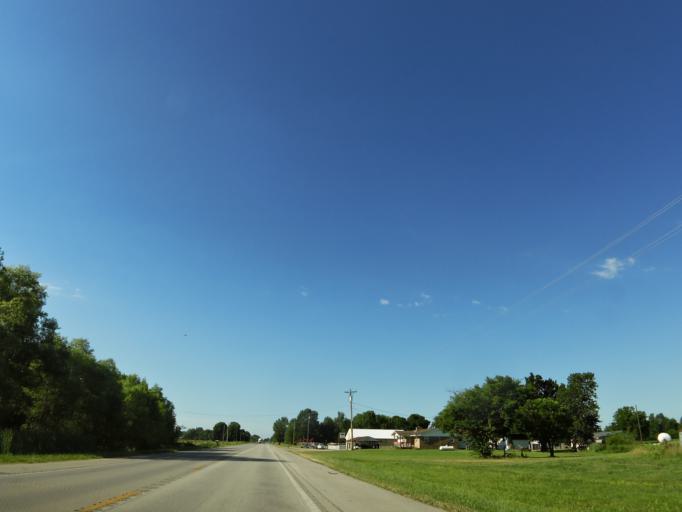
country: US
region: Arkansas
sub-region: Clay County
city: Corning
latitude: 36.5721
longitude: -90.5209
